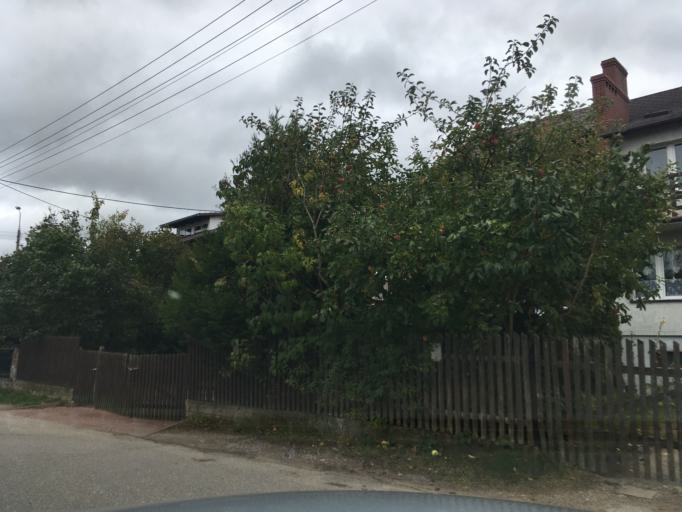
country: PL
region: Pomeranian Voivodeship
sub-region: Powiat koscierski
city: Koscierzyna
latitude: 54.1152
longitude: 18.0005
